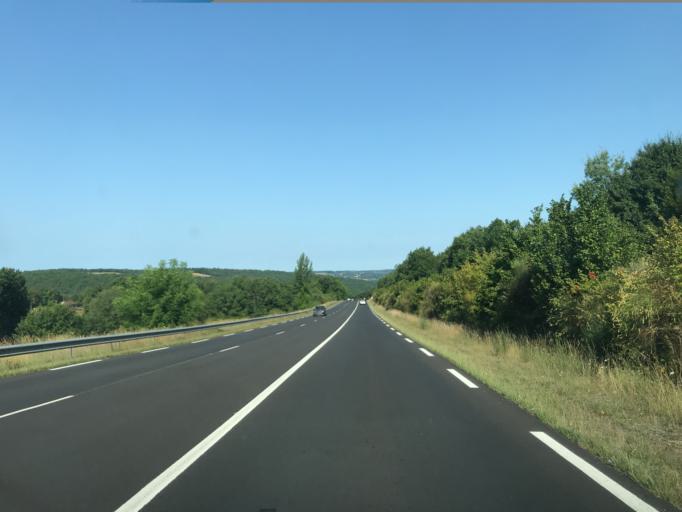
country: FR
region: Aquitaine
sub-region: Departement de la Dordogne
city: Montignac
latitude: 45.0462
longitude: 1.2243
